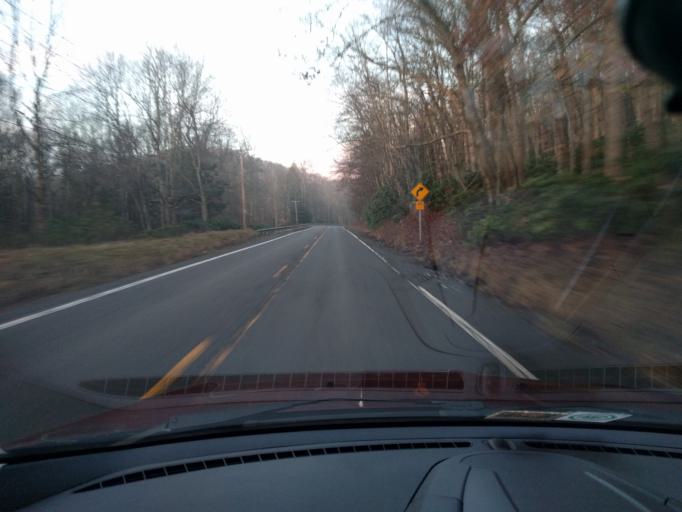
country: US
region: West Virginia
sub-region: Fayette County
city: Fayetteville
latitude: 38.0489
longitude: -80.9364
